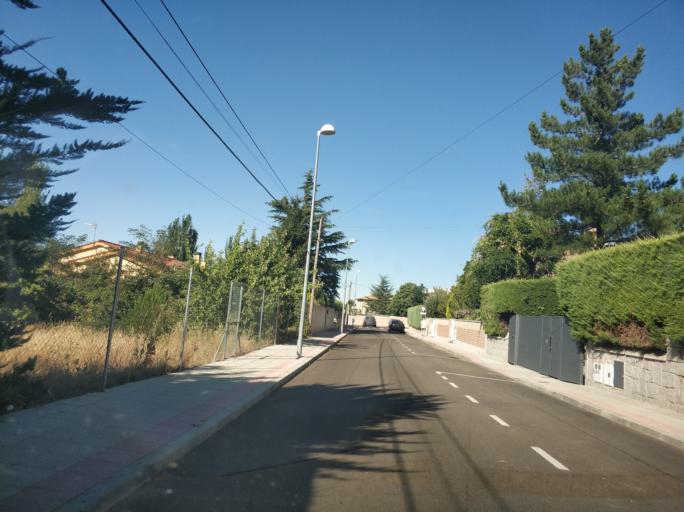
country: ES
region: Castille and Leon
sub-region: Provincia de Salamanca
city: Santa Marta de Tormes
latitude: 40.9400
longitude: -5.6226
